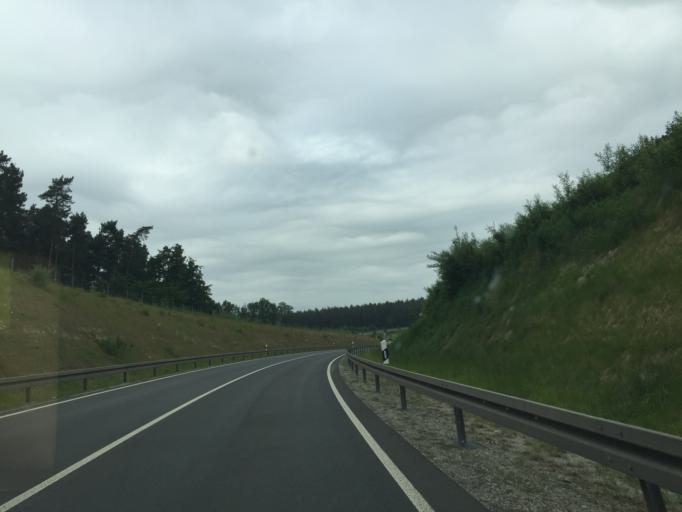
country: DE
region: Thuringia
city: Langewiesen
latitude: 50.7001
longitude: 10.9637
